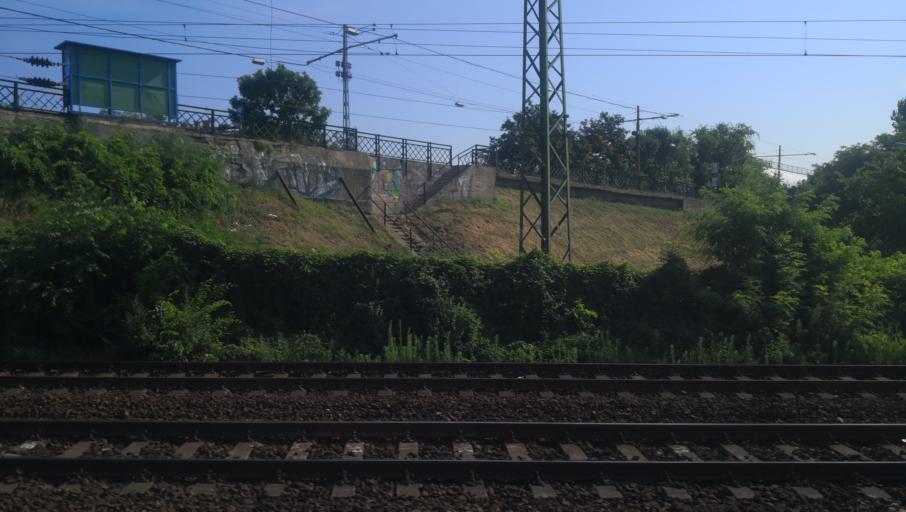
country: HU
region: Budapest
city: Budapest XIV. keruelet
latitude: 47.4893
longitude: 19.1047
